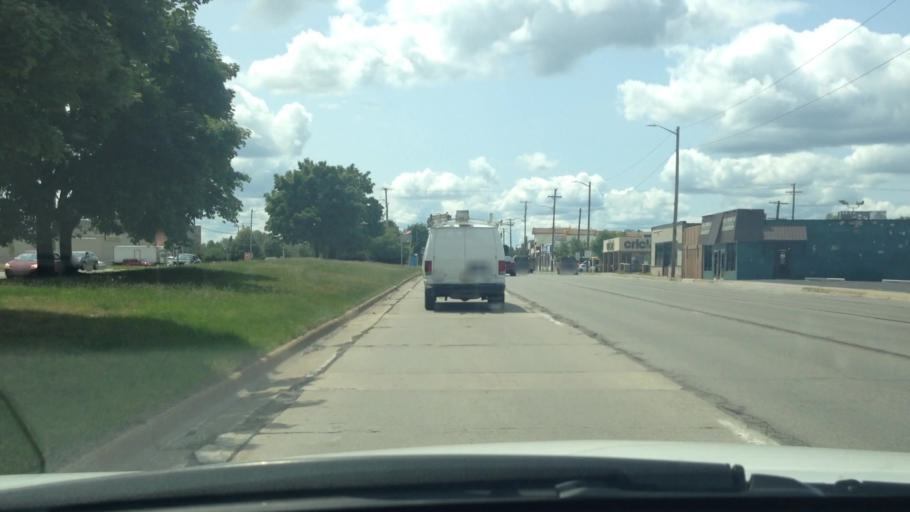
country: US
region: Michigan
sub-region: Wayne County
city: Inkster
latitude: 42.2946
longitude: -83.3083
